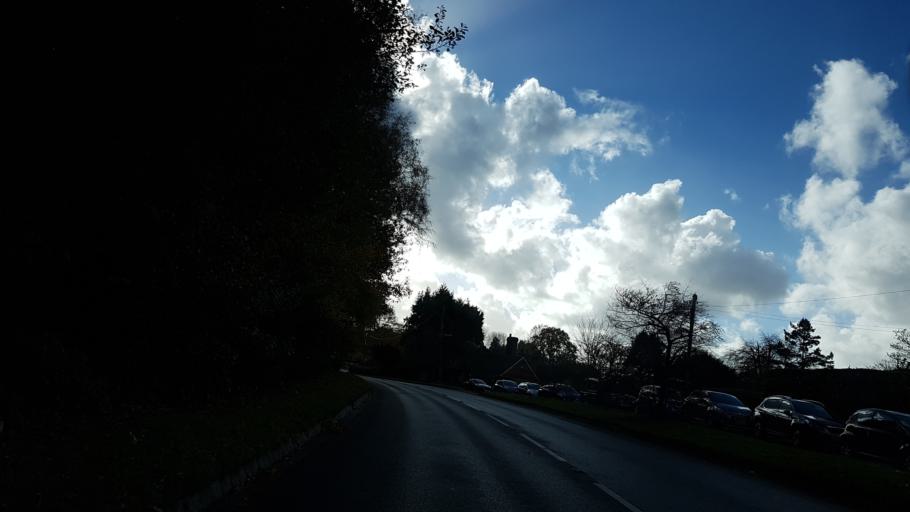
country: GB
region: England
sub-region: Surrey
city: Milford
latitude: 51.1365
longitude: -0.6725
